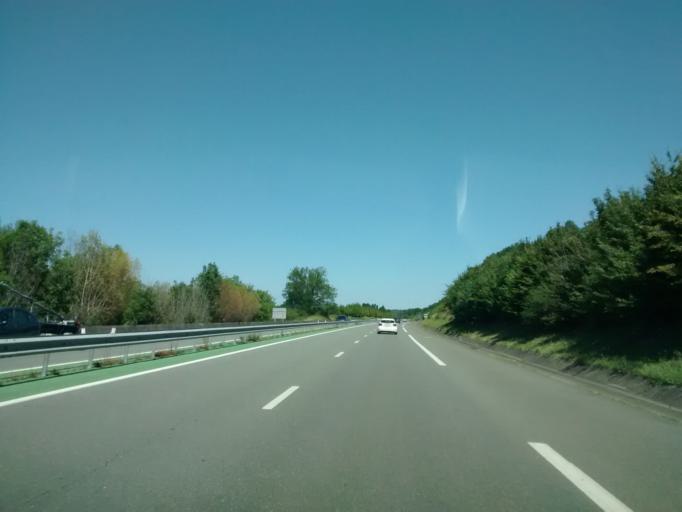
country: FR
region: Aquitaine
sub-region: Departement de la Dordogne
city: Neuvic
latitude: 45.0704
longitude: 0.4384
